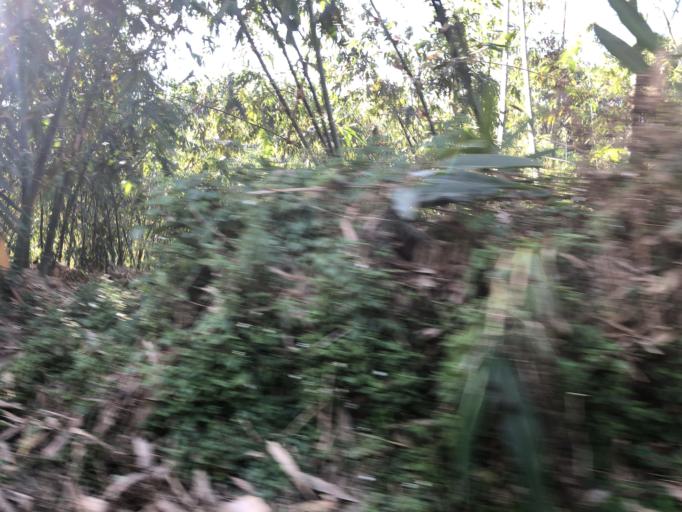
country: TW
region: Taiwan
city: Yujing
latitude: 23.0117
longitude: 120.3856
